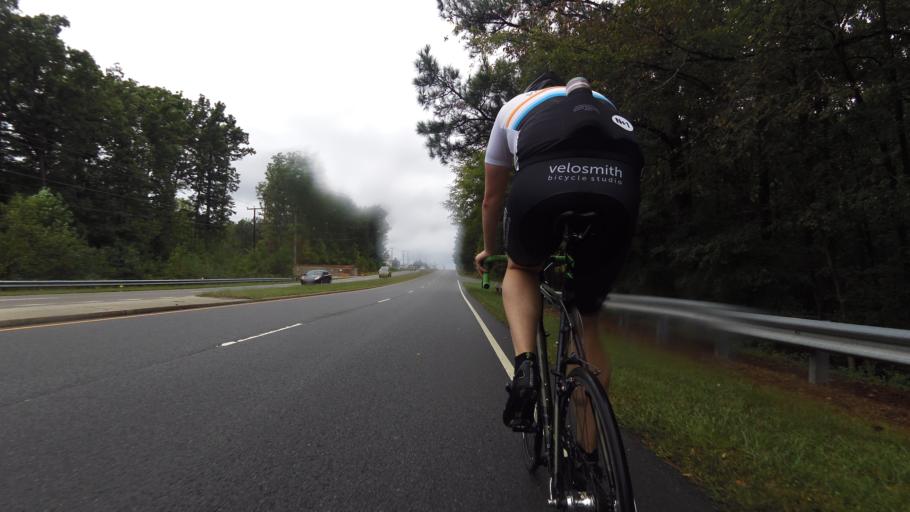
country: US
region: Virginia
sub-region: Henrico County
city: Short Pump
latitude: 37.5988
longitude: -77.6432
